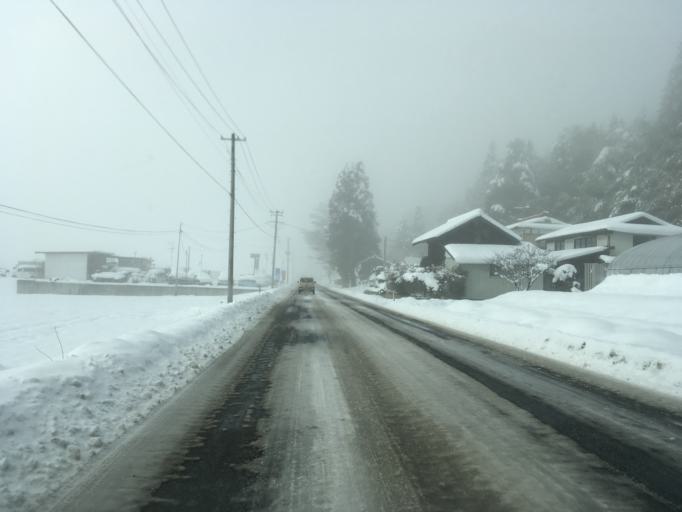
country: JP
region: Iwate
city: Ichinoseki
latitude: 38.8629
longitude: 141.1506
